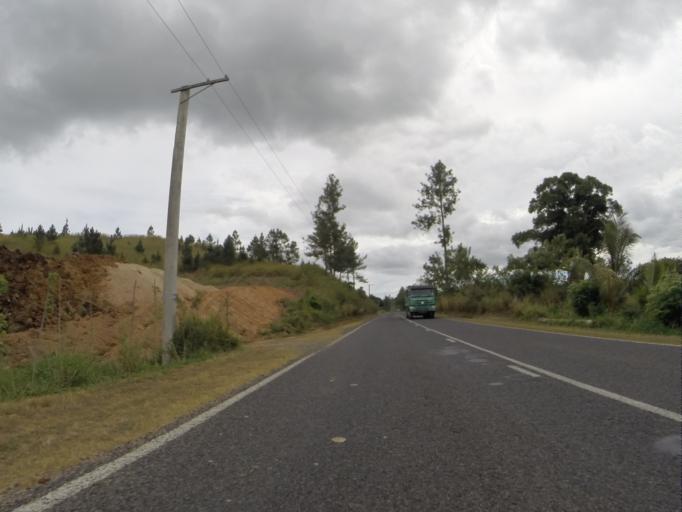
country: FJ
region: Western
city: Nadi
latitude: -18.0075
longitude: 177.3208
